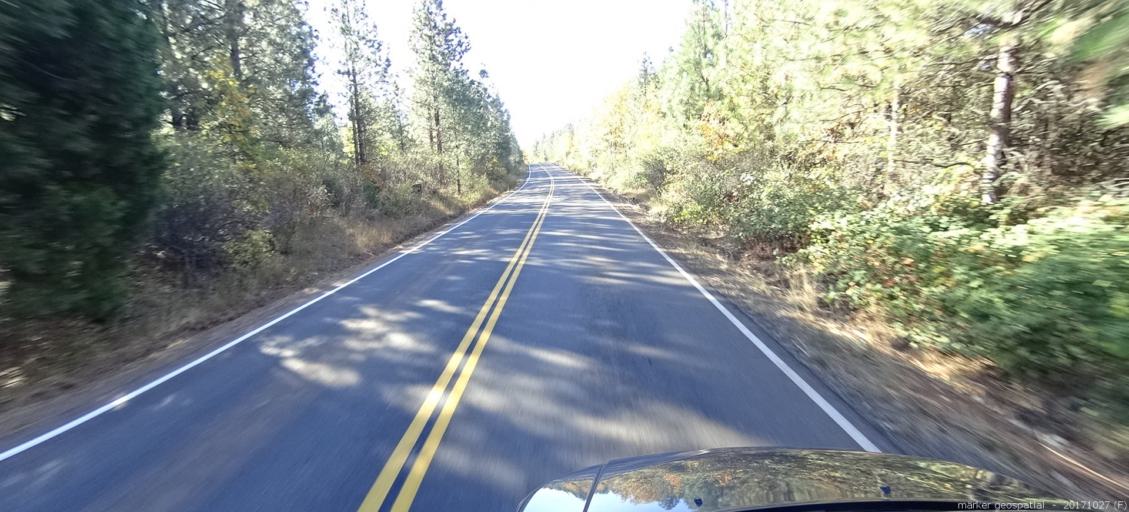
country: US
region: California
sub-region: Shasta County
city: Burney
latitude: 40.8852
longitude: -121.9084
